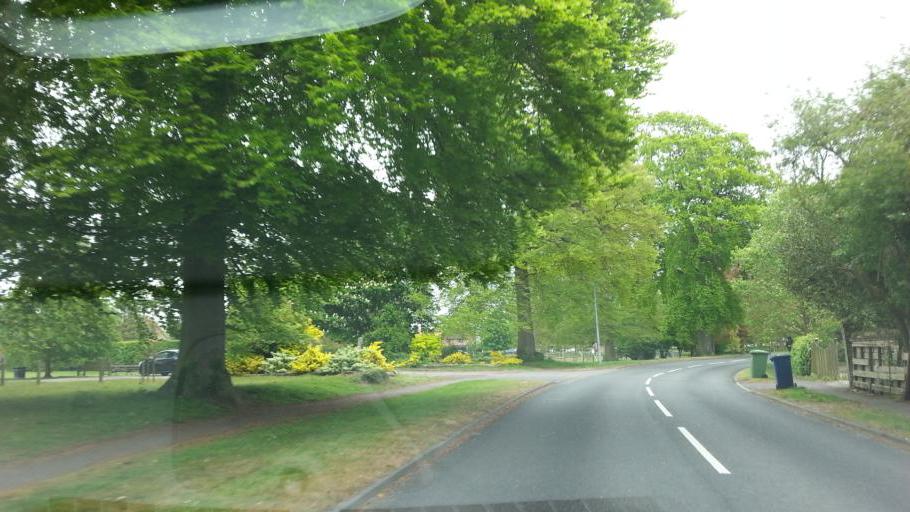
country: GB
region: England
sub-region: Cambridgeshire
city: Sawston
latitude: 52.1129
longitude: 0.1515
